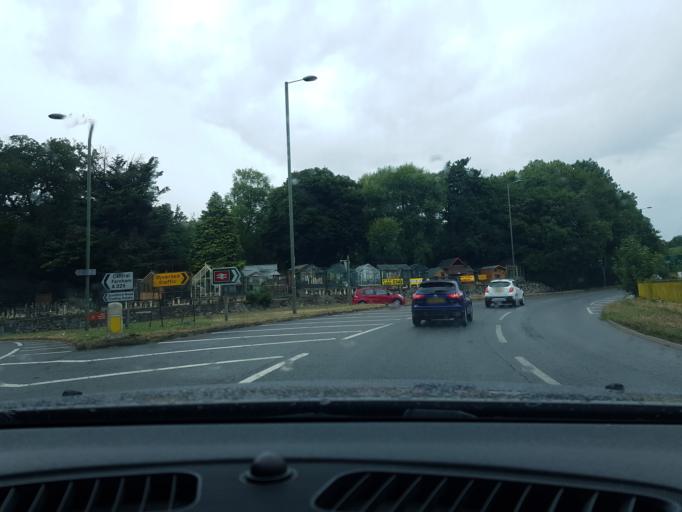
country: GB
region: England
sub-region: Surrey
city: Hale
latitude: 51.2192
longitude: -0.7800
